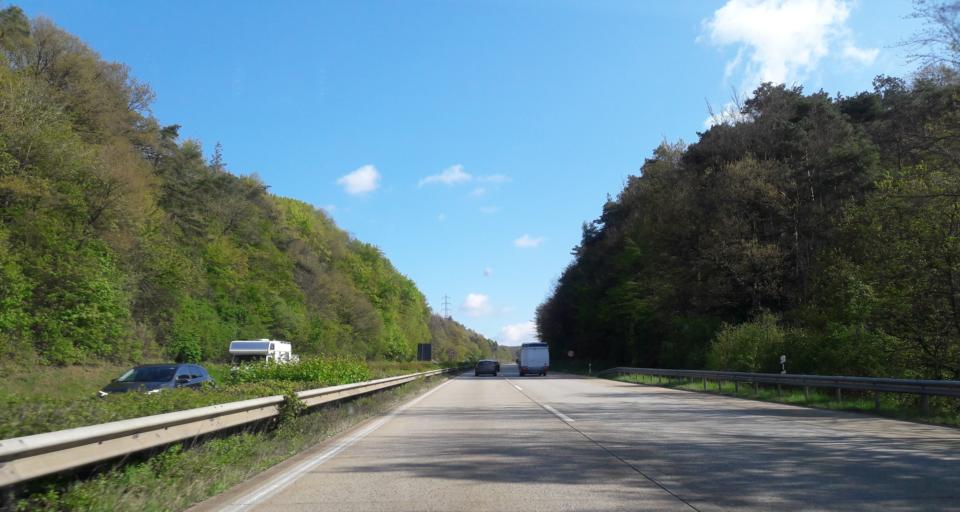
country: DE
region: Rheinland-Pfalz
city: Flussbach
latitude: 50.0065
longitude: 6.9320
